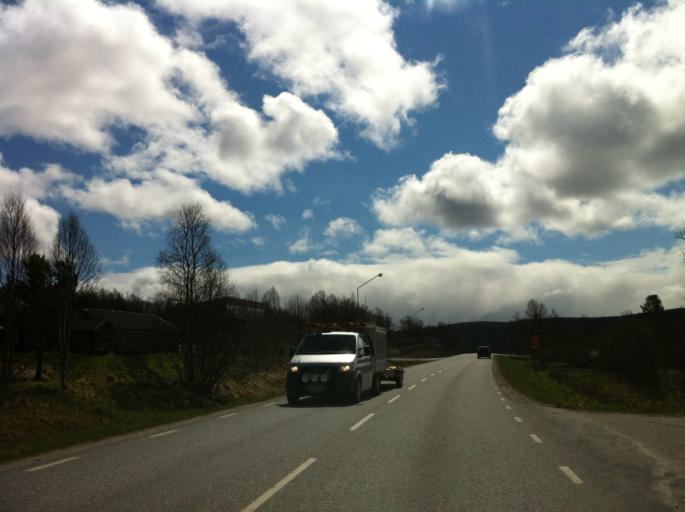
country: NO
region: Sor-Trondelag
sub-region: Tydal
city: Aas
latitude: 62.6370
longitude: 12.4446
